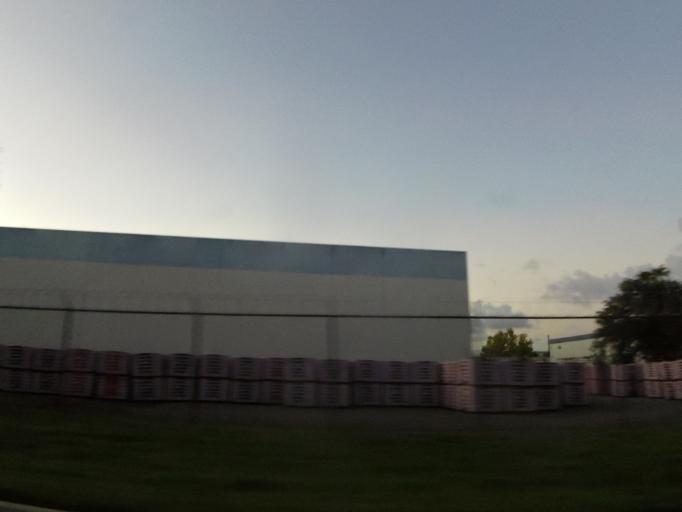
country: US
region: Florida
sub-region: Duval County
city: Jacksonville
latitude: 30.3316
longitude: -81.6338
